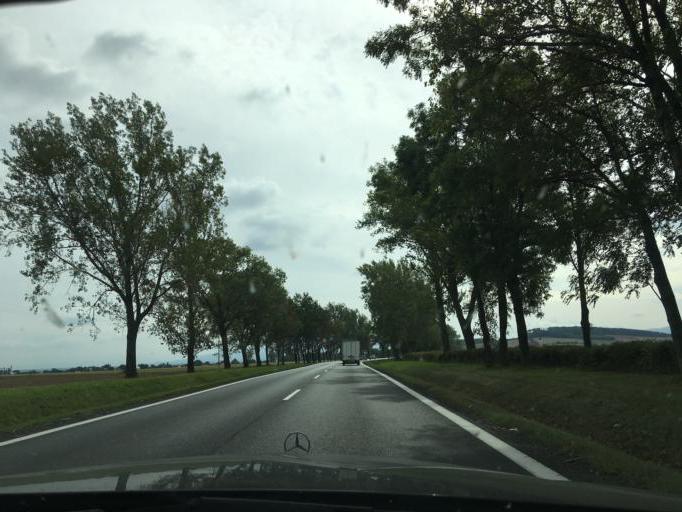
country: PL
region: Lower Silesian Voivodeship
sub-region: Powiat zabkowicki
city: Zabkowice Slaskie
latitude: 50.5647
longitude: 16.7901
